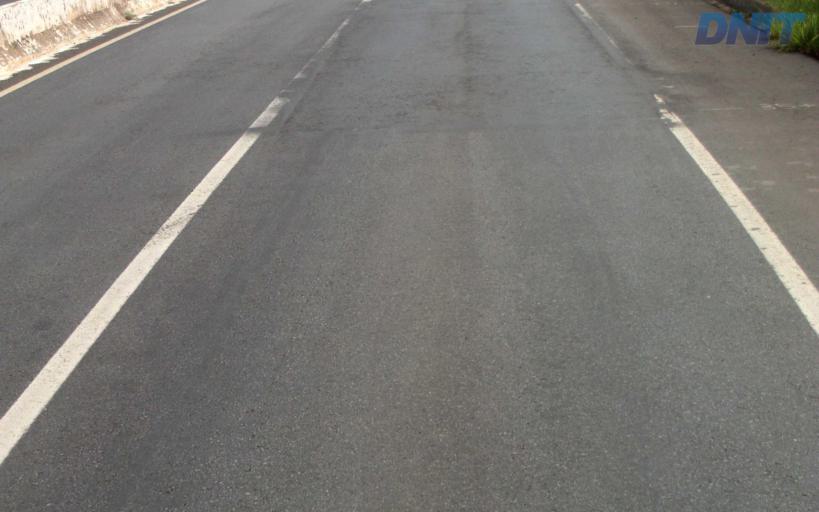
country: BR
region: Minas Gerais
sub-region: Ipaba
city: Ipaba
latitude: -19.3095
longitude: -42.3918
